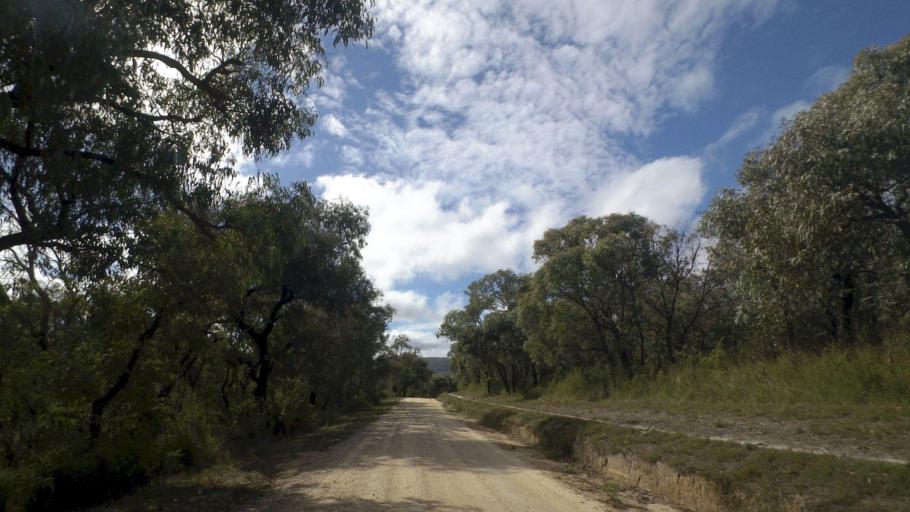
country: AU
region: Victoria
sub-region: Cardinia
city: Gembrook
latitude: -37.9938
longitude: 145.6189
